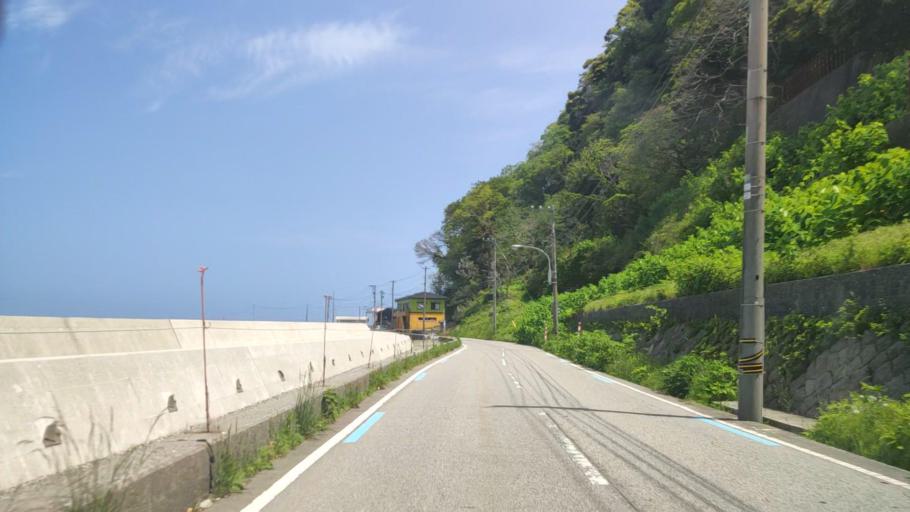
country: JP
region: Toyama
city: Nyuzen
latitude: 36.9710
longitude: 137.5851
